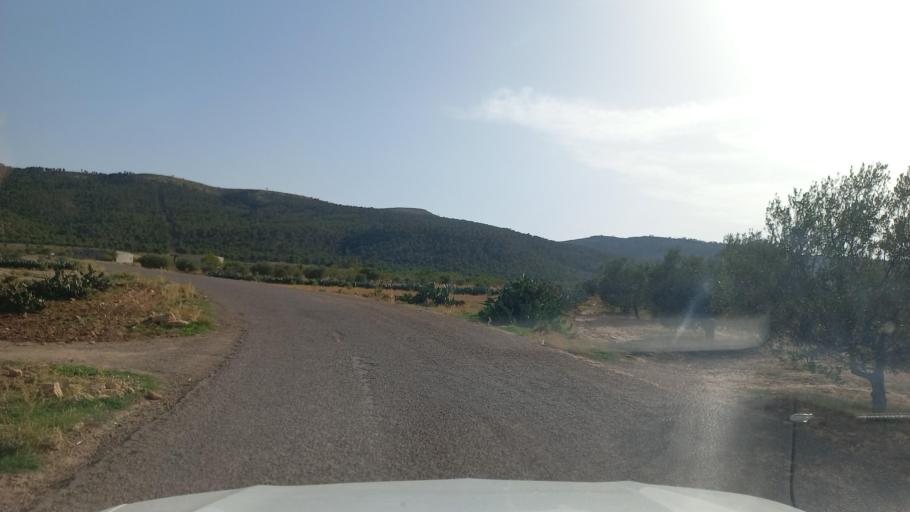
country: TN
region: Al Qasrayn
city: Kasserine
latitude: 35.3418
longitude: 8.8348
